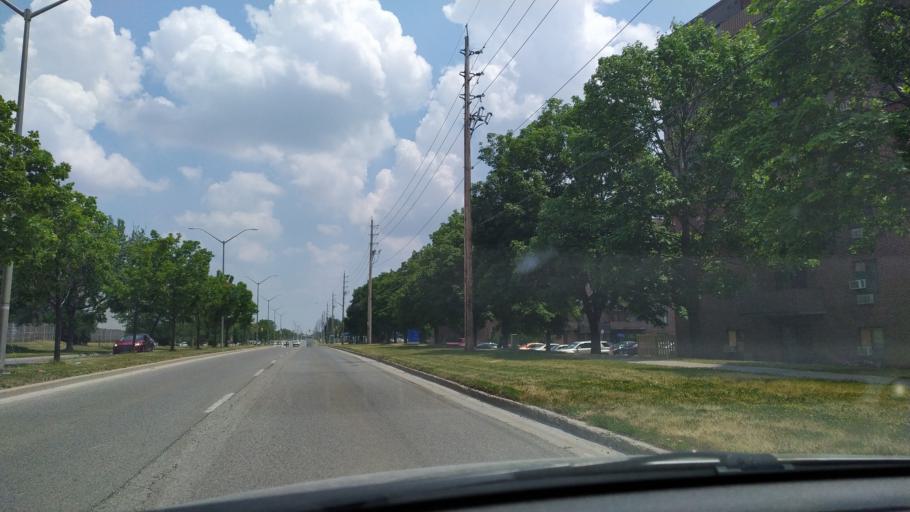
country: CA
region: Ontario
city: London
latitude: 42.9343
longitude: -81.2398
